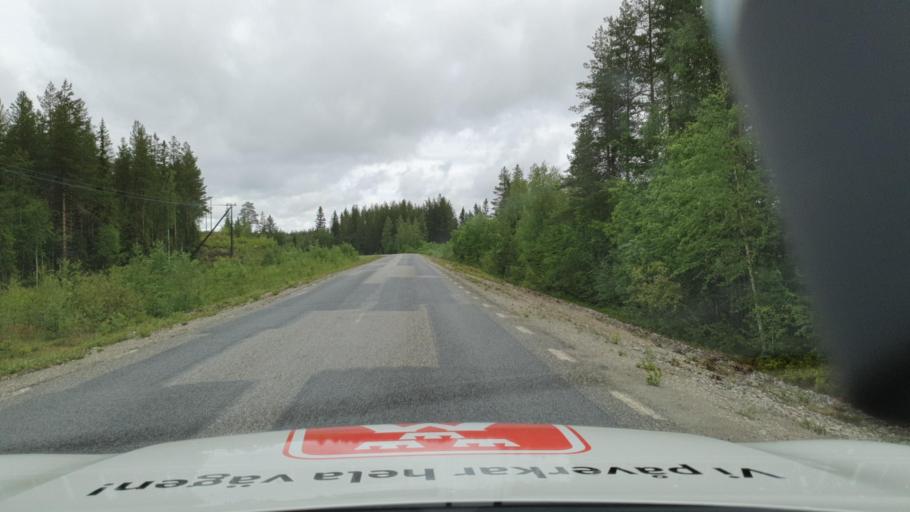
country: SE
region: Vaesterbotten
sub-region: Dorotea Kommun
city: Dorotea
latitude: 64.1379
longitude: 16.6421
